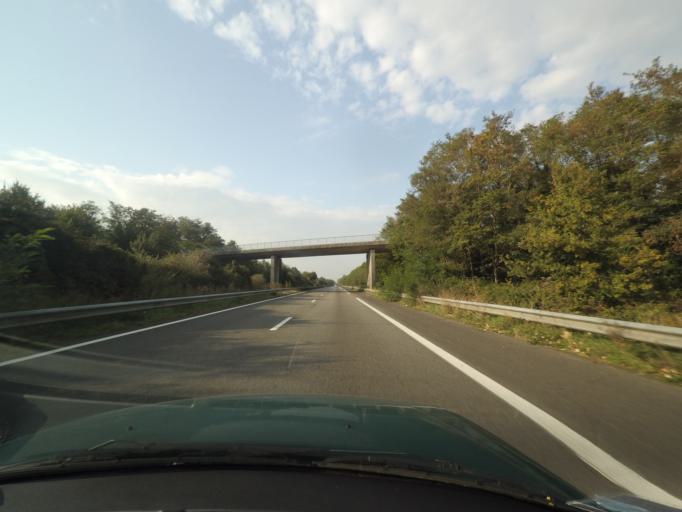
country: FR
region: Pays de la Loire
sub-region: Departement de la Loire-Atlantique
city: Jans
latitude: 47.6084
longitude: -1.6296
